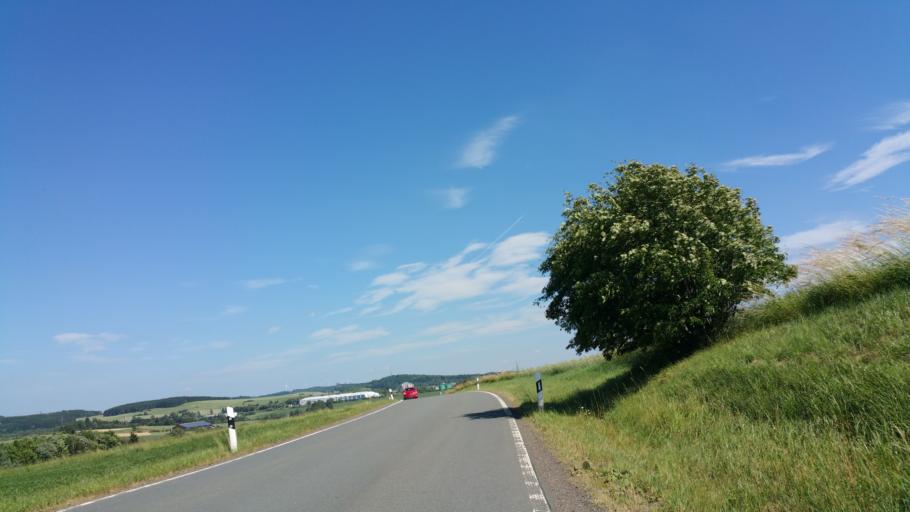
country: DE
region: Bavaria
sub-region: Upper Franconia
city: Koditz
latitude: 50.3424
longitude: 11.8813
